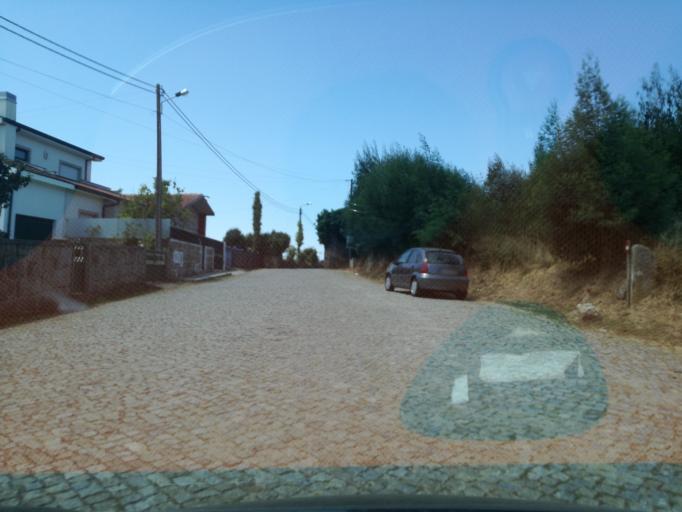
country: PT
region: Porto
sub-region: Maia
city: Anta
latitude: 41.2500
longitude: -8.6339
